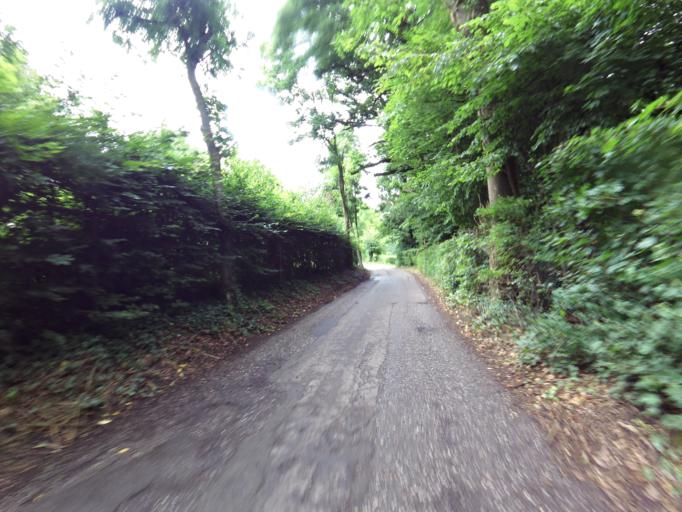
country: NL
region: Limburg
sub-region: Gemeente Kerkrade
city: Kerkrade
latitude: 50.8859
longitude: 6.0323
